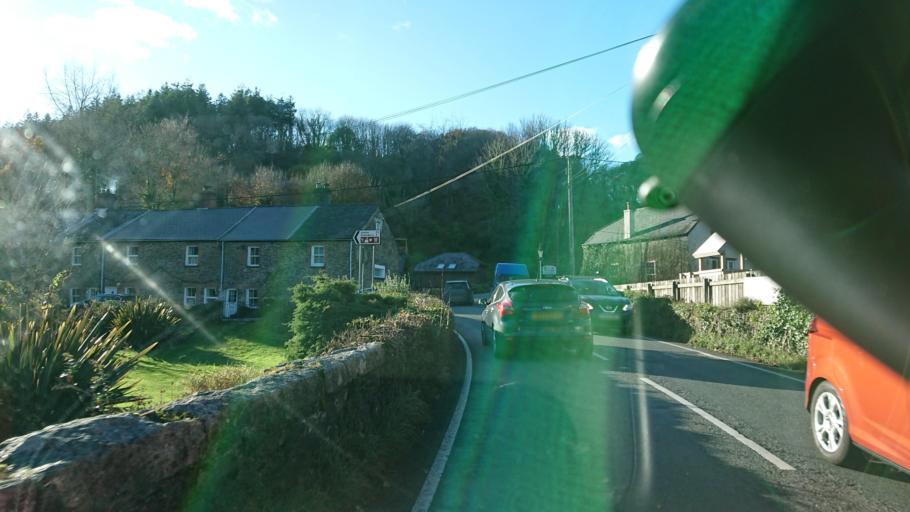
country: GB
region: England
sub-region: Cornwall
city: Looe
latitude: 50.3919
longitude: -4.3828
